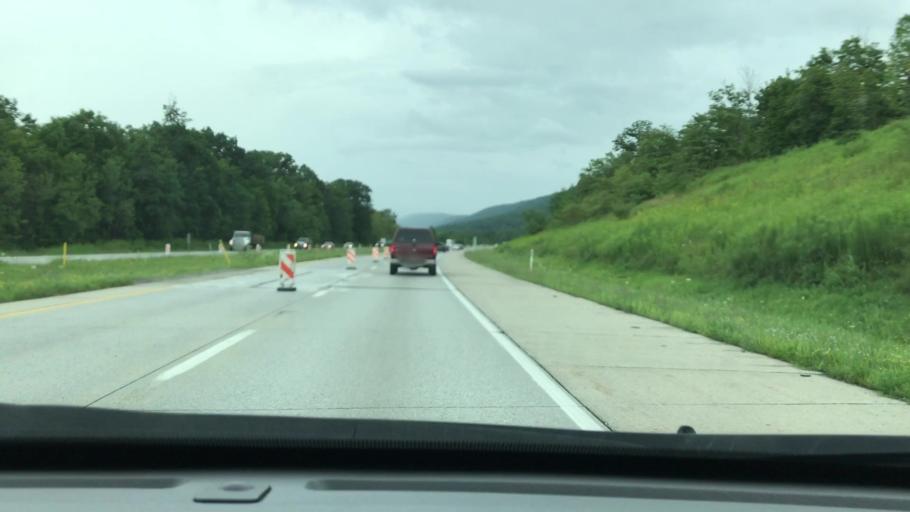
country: US
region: Pennsylvania
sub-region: Blair County
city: Tipton
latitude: 40.6163
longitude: -78.3032
